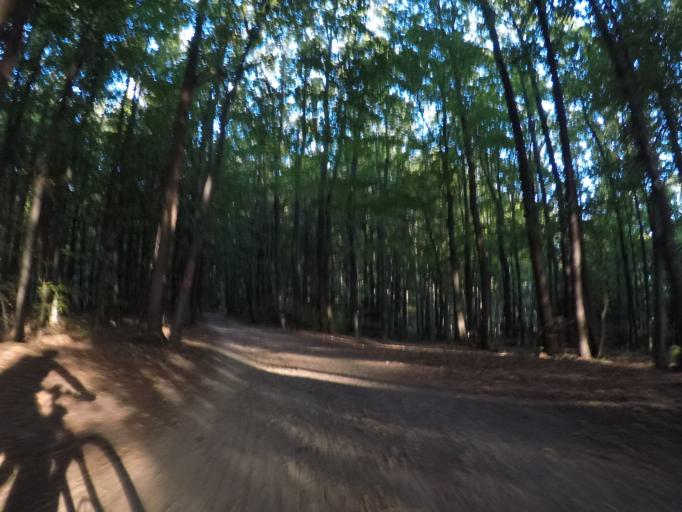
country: SK
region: Kosicky
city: Kosice
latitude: 48.7450
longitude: 21.1925
